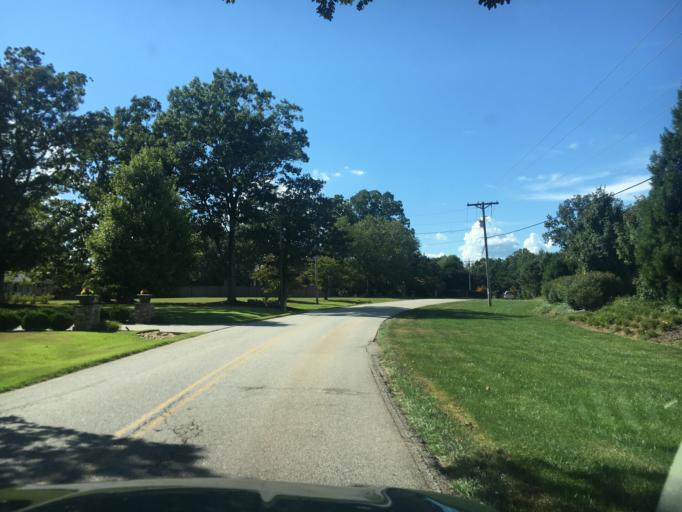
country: US
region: South Carolina
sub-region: Greenville County
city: Five Forks
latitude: 34.8202
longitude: -82.2207
